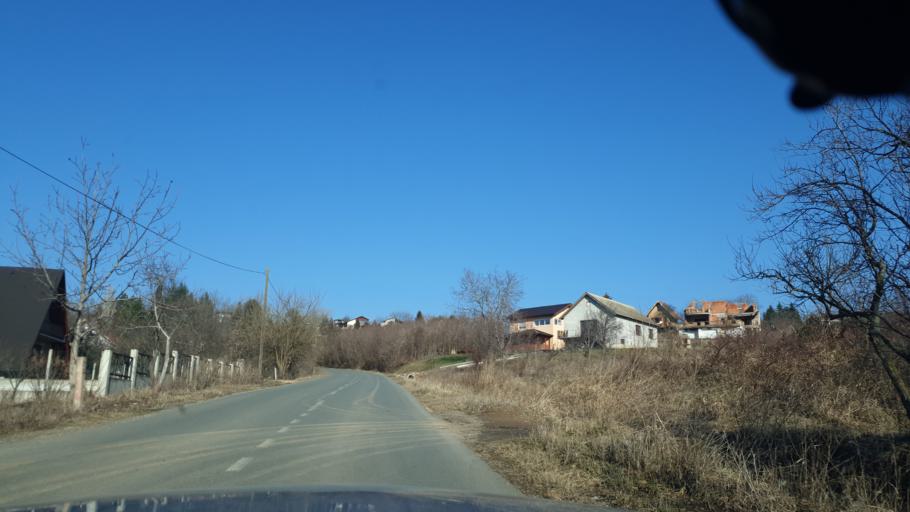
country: RS
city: Vrdnik
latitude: 45.1147
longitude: 19.7728
